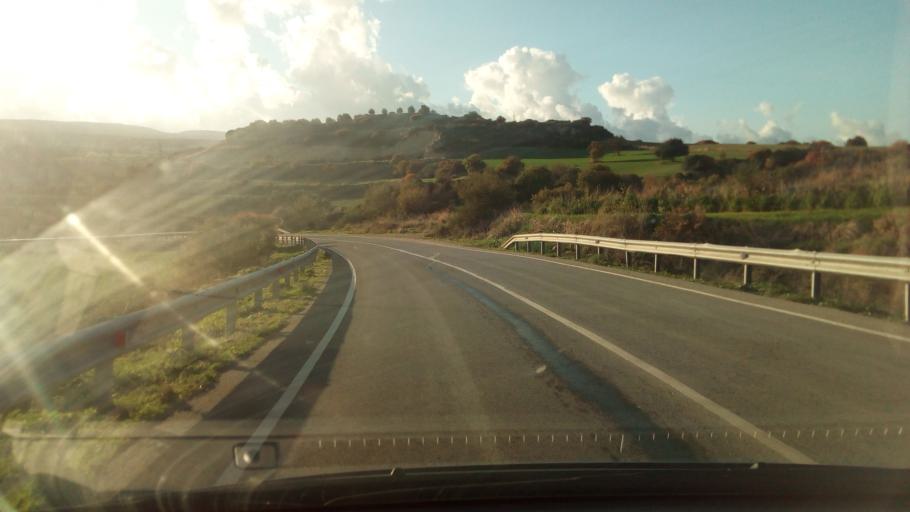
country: CY
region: Pafos
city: Polis
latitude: 34.9589
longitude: 32.4762
